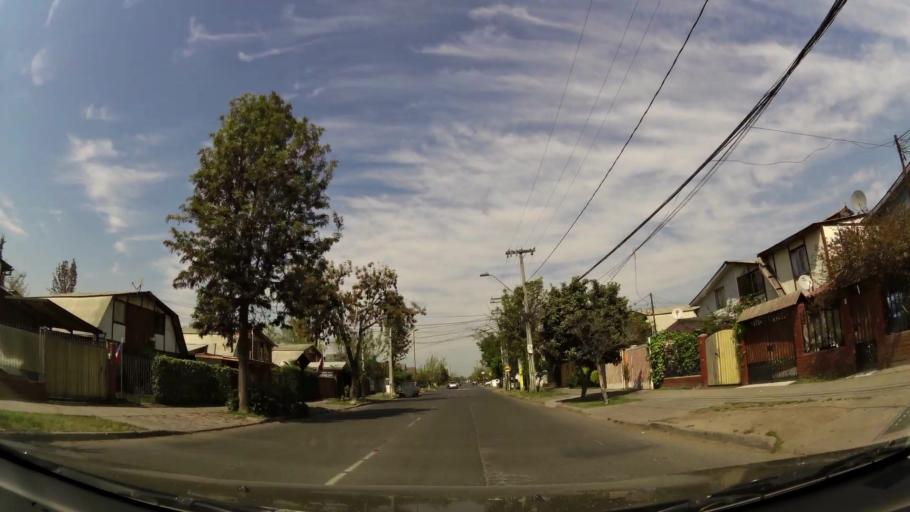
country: CL
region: Santiago Metropolitan
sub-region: Provincia de Cordillera
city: Puente Alto
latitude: -33.5912
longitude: -70.5856
